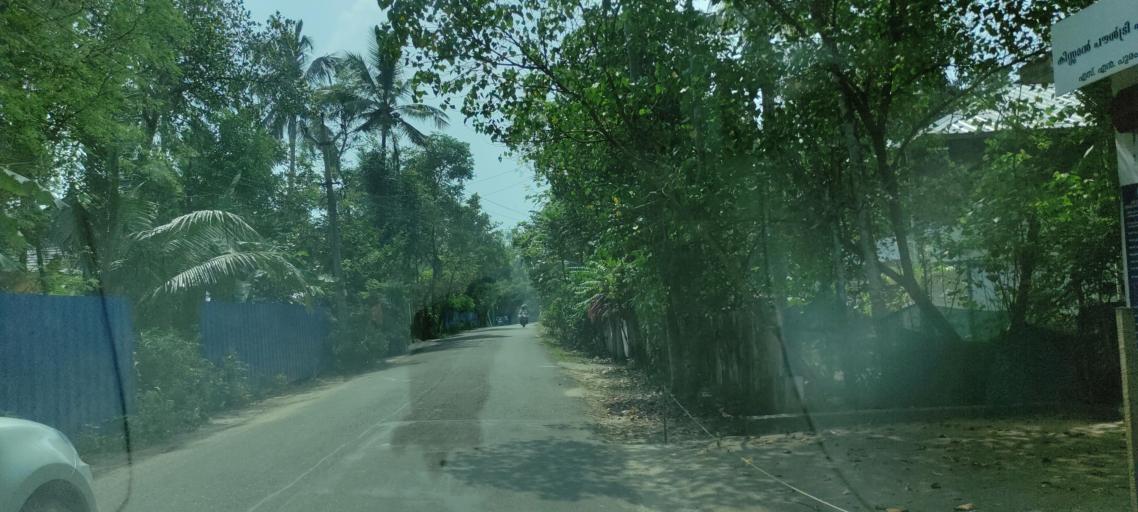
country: IN
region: Kerala
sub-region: Alappuzha
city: Shertallai
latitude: 9.6213
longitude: 76.3489
